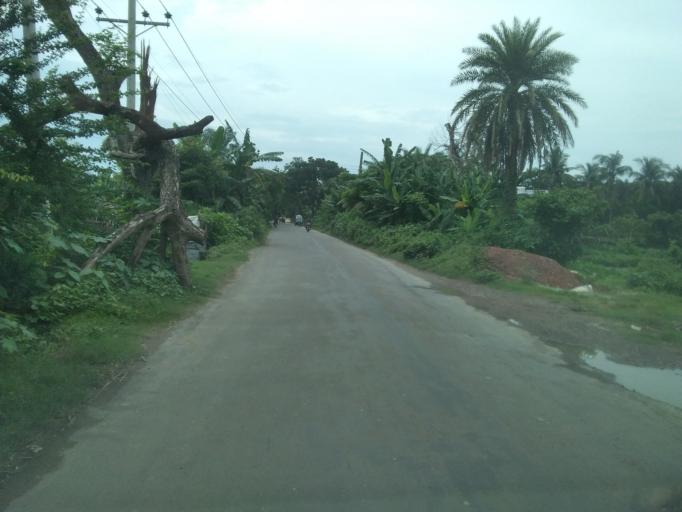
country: IN
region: West Bengal
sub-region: North 24 Parganas
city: Taki
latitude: 22.5786
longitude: 88.9984
